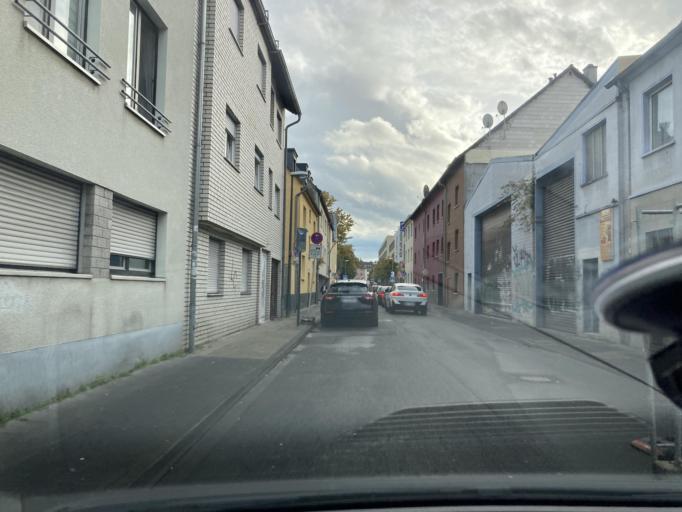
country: DE
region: North Rhine-Westphalia
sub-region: Regierungsbezirk Koln
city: Kalk
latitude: 50.9402
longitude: 6.9996
